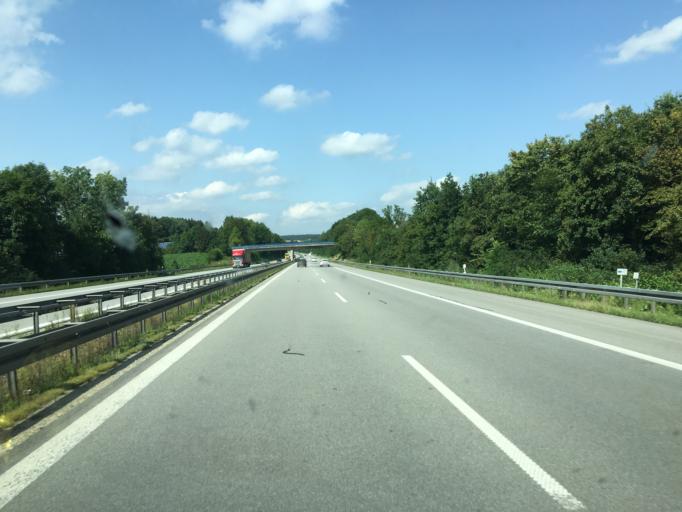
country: DE
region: Bavaria
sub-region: Lower Bavaria
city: Furstenzell
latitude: 48.5023
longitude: 13.3830
